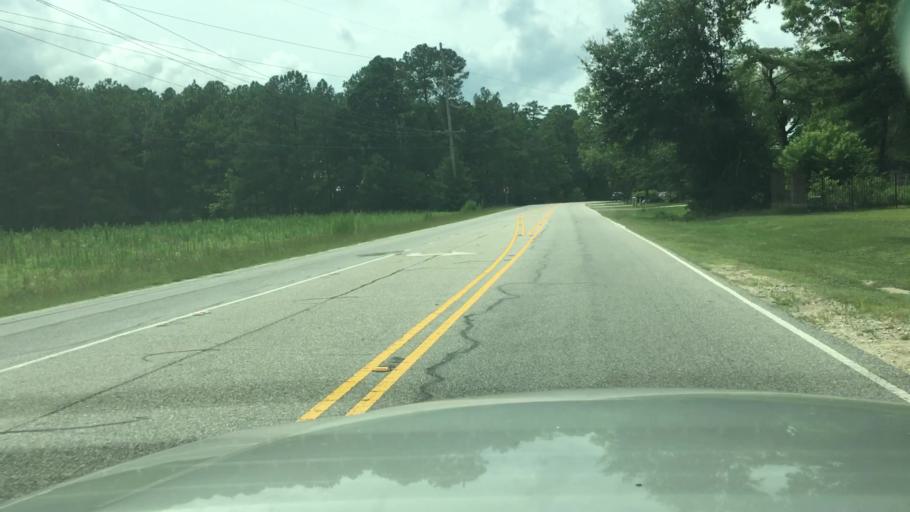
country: US
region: North Carolina
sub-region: Cumberland County
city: Hope Mills
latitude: 35.0036
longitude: -78.9944
